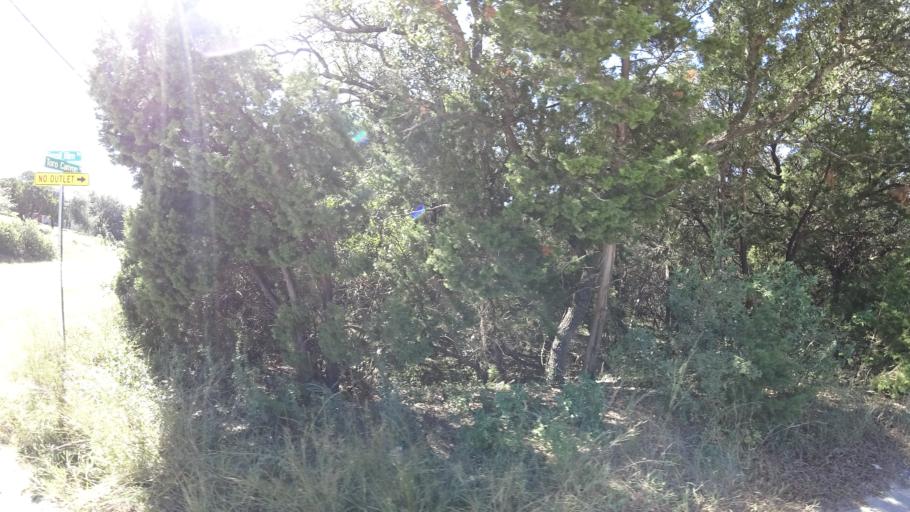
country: US
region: Texas
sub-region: Travis County
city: West Lake Hills
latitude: 30.3218
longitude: -97.7946
